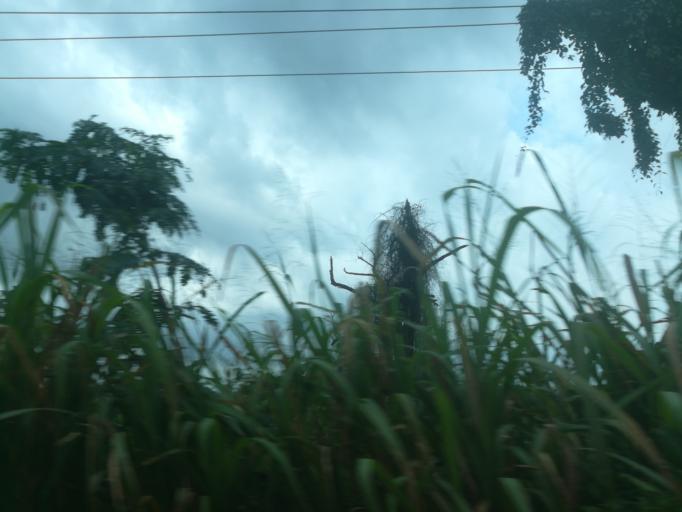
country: NG
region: Lagos
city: Ikorodu
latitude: 6.6639
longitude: 3.6124
